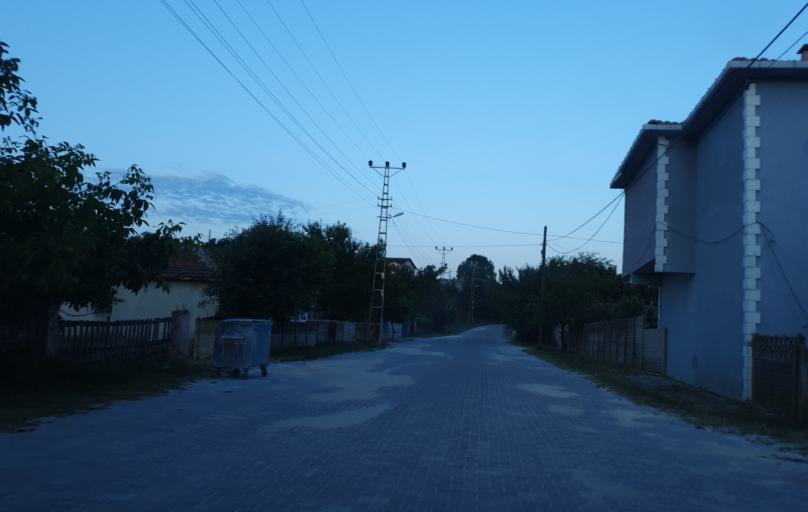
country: TR
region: Tekirdag
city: Velimese
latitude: 41.3507
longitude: 27.8792
